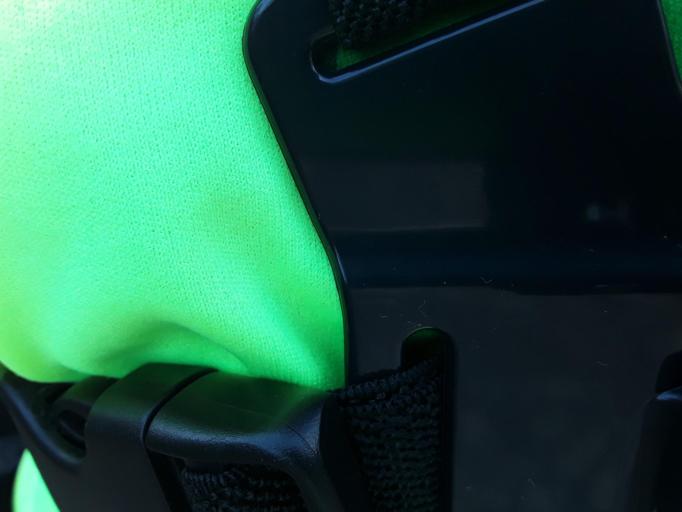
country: BR
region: Minas Gerais
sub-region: Lima Duarte
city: Lima Duarte
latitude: -21.7125
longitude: -43.8987
